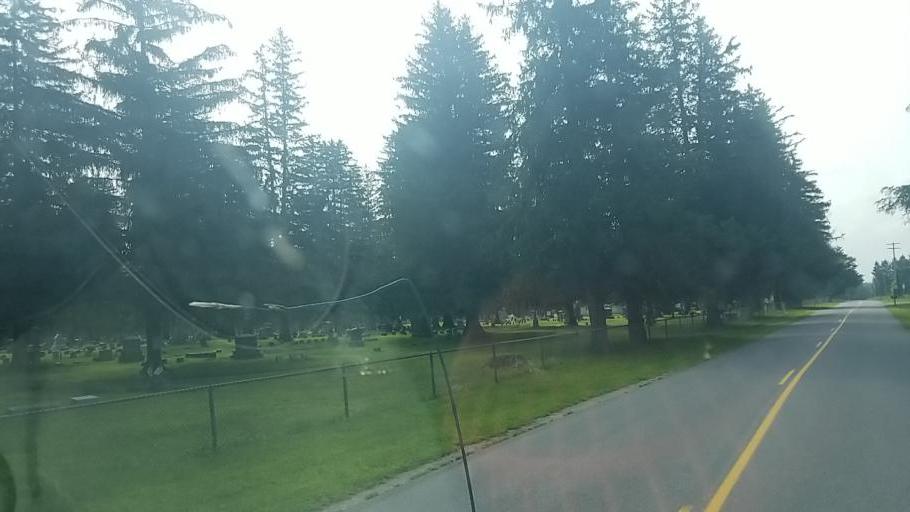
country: US
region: New York
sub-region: Montgomery County
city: Fonda
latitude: 42.9566
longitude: -74.4154
